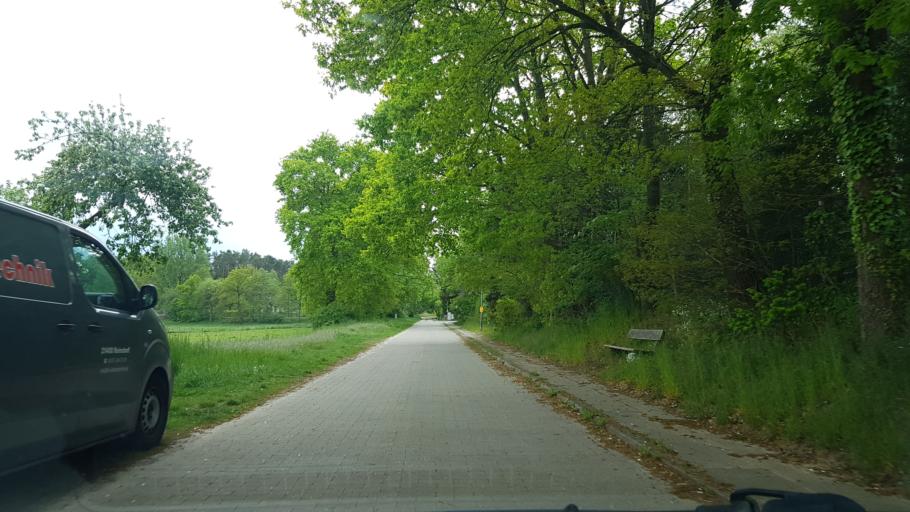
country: DE
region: Lower Saxony
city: Vastorf
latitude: 53.1998
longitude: 10.5432
